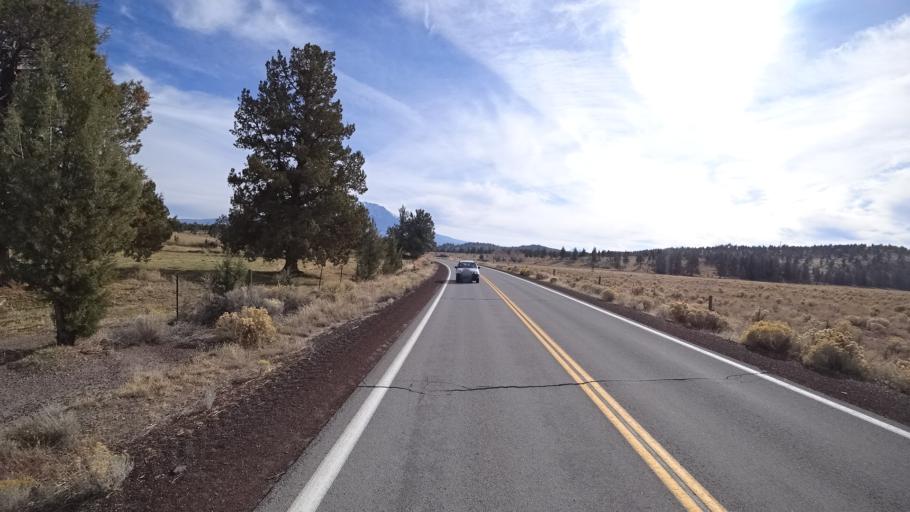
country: US
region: California
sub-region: Siskiyou County
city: Weed
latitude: 41.5569
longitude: -122.3865
